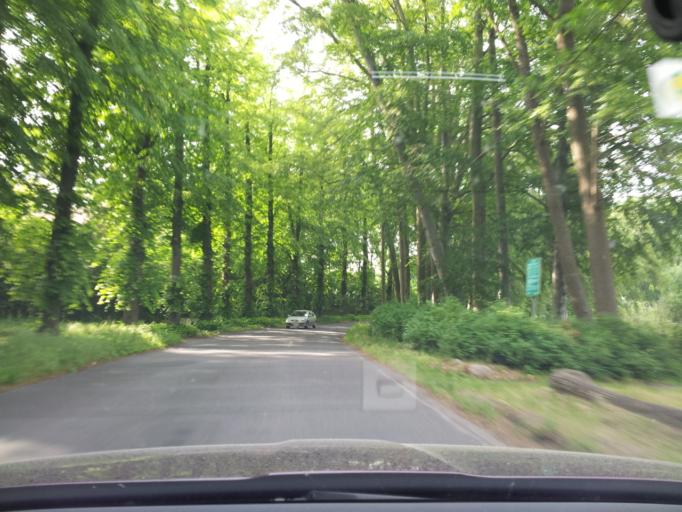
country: DE
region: Brandenburg
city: Werder
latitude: 52.3431
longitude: 12.9401
